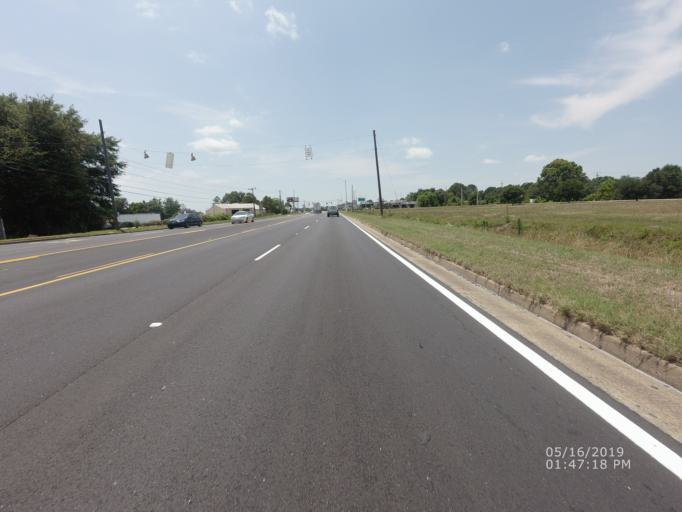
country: US
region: Georgia
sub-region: Dougherty County
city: Albany
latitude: 31.5491
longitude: -84.1727
